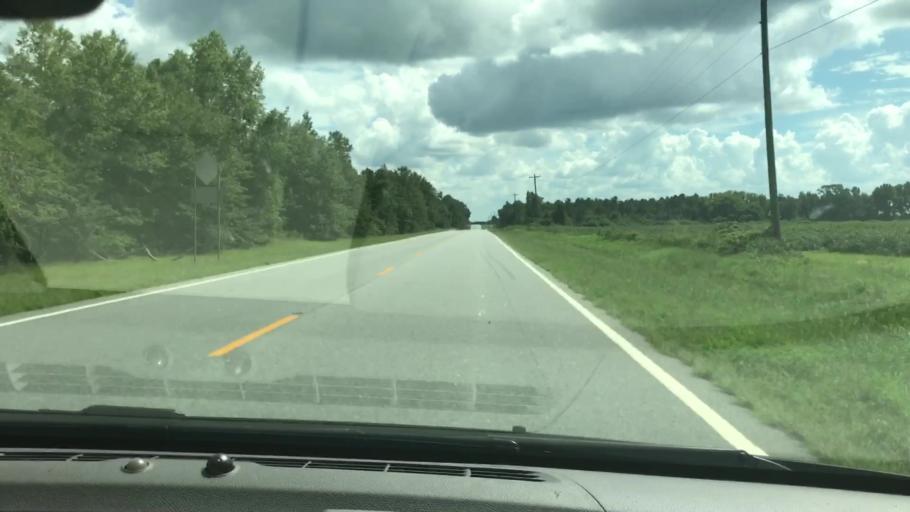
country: US
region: Georgia
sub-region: Quitman County
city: Georgetown
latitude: 31.7954
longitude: -85.0924
